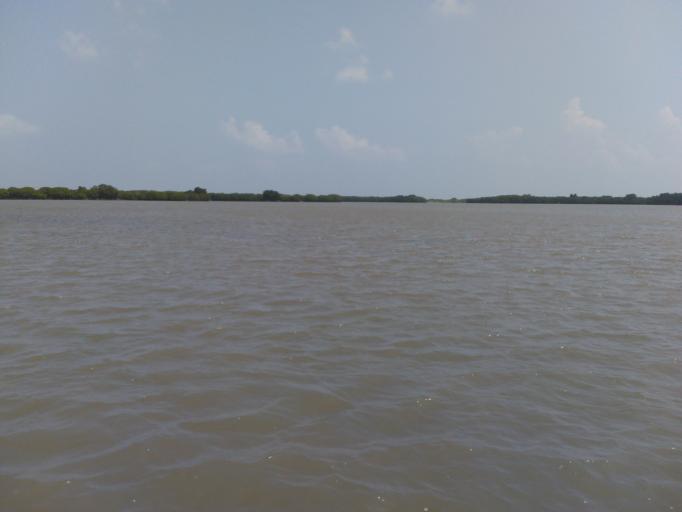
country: IN
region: Tamil Nadu
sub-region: Cuddalore
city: Annamalainagar
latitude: 11.4422
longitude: 79.7914
